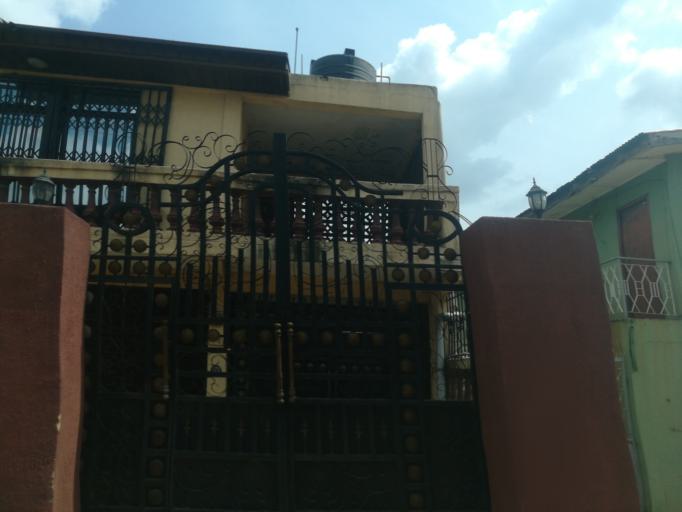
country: NG
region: Oyo
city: Ibadan
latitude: 7.3565
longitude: 3.8788
